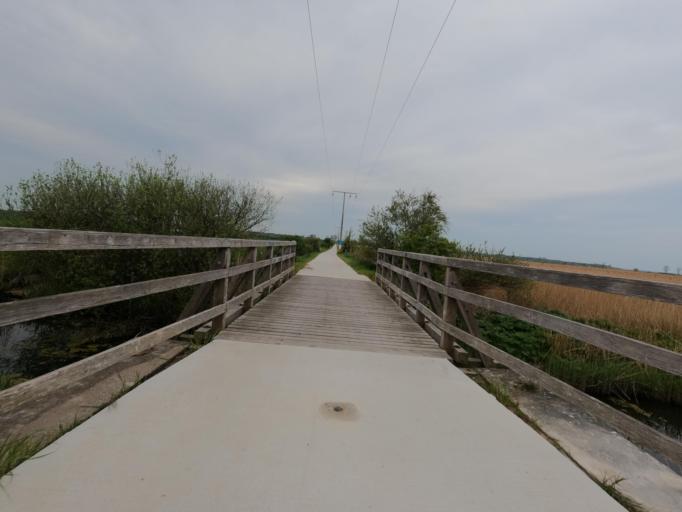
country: DE
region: Mecklenburg-Vorpommern
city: Saal
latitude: 54.3058
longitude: 12.5009
